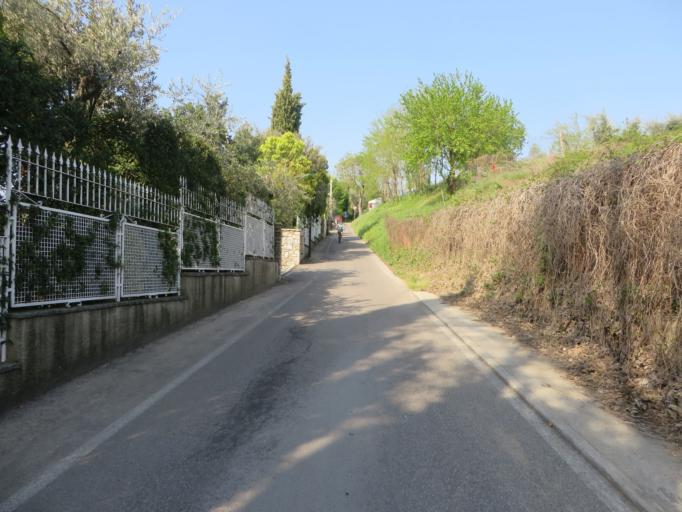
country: IT
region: Lombardy
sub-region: Provincia di Brescia
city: Solarolo
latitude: 45.5443
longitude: 10.5645
